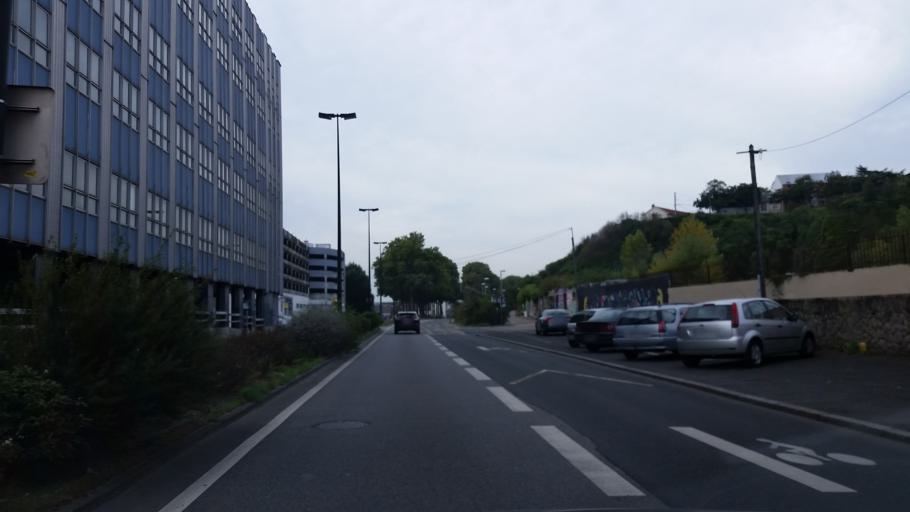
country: FR
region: Pays de la Loire
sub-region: Departement de la Loire-Atlantique
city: Nantes
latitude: 47.2003
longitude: -1.5789
